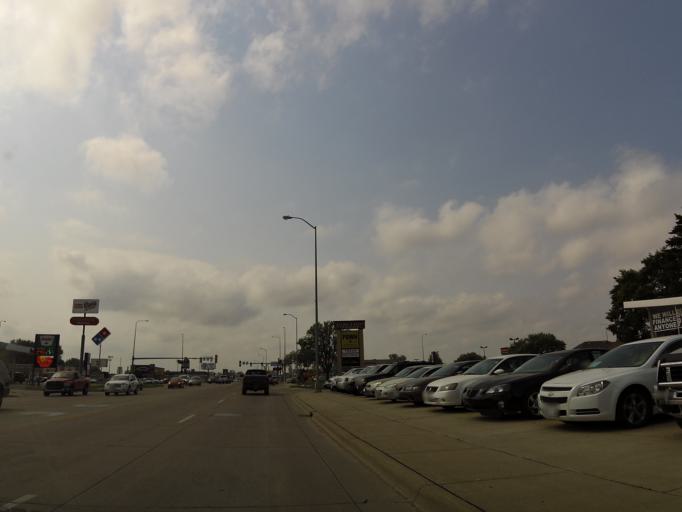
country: US
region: South Dakota
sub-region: Codington County
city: Watertown
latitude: 44.8902
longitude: -97.1076
